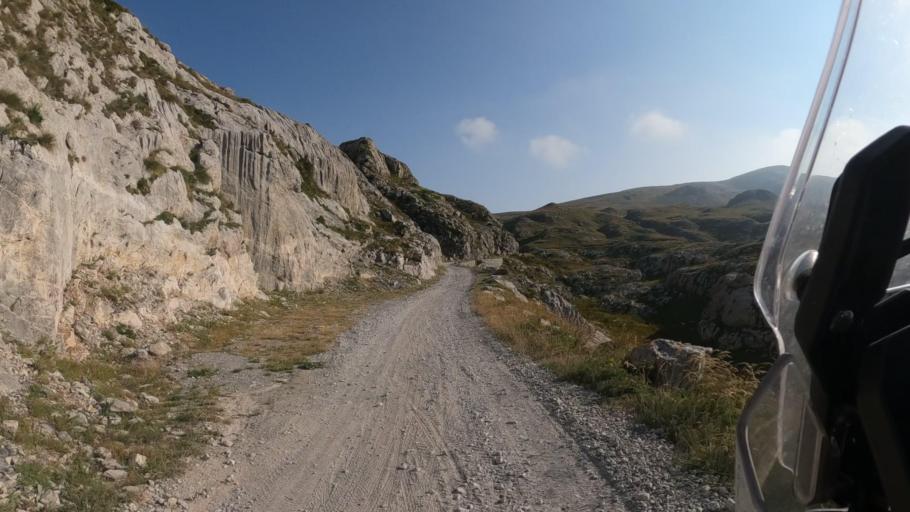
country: IT
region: Piedmont
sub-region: Provincia di Cuneo
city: Limone Piemonte
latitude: 44.1723
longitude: 7.6364
